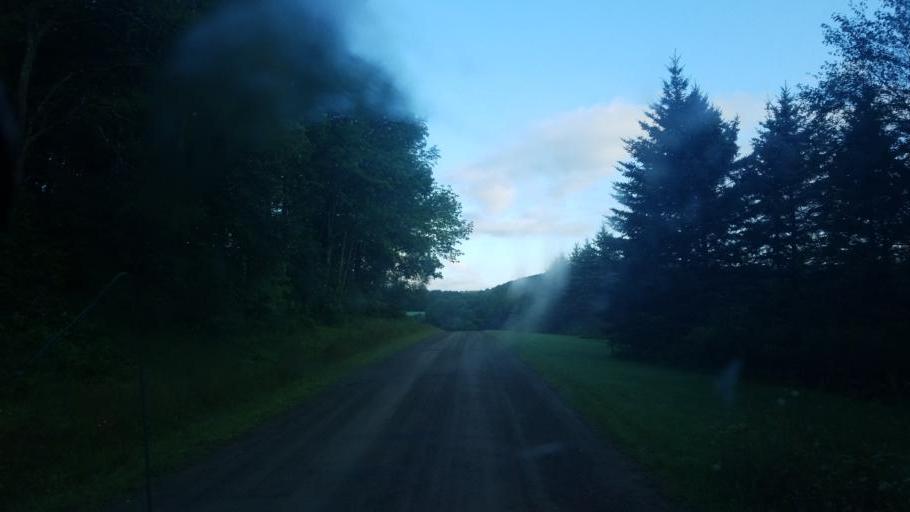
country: US
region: Pennsylvania
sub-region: Potter County
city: Galeton
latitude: 41.8776
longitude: -77.8089
